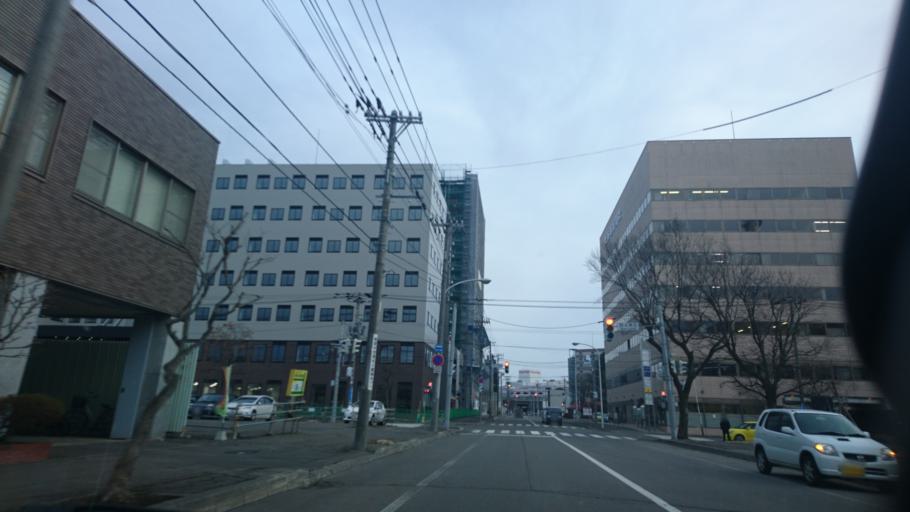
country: JP
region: Hokkaido
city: Obihiro
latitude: 42.9228
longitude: 143.1989
